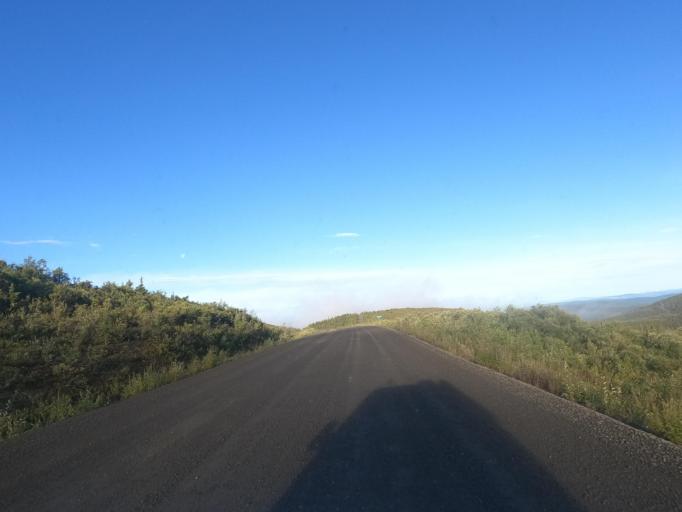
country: CA
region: Yukon
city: Dawson City
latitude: 64.2203
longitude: -140.3099
